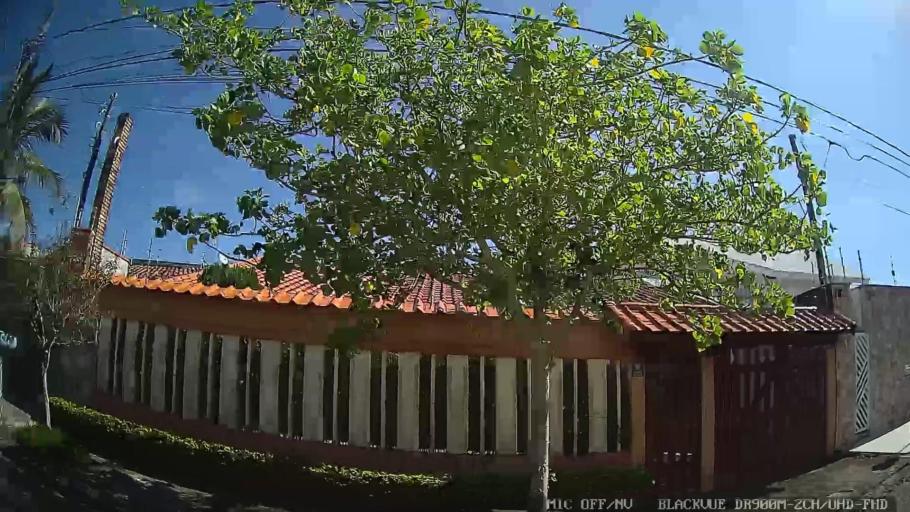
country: BR
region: Sao Paulo
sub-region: Peruibe
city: Peruibe
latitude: -24.2910
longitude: -46.9699
